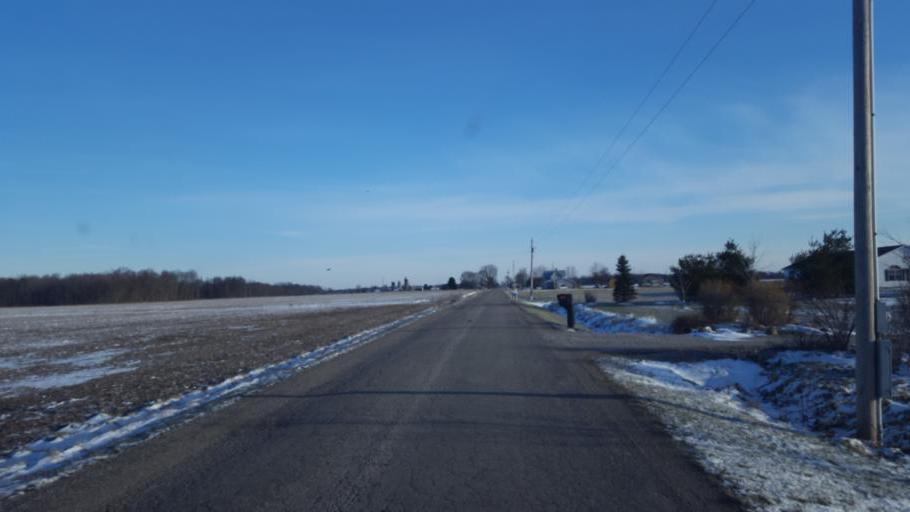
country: US
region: Ohio
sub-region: Morrow County
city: Cardington
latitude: 40.5595
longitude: -82.9384
